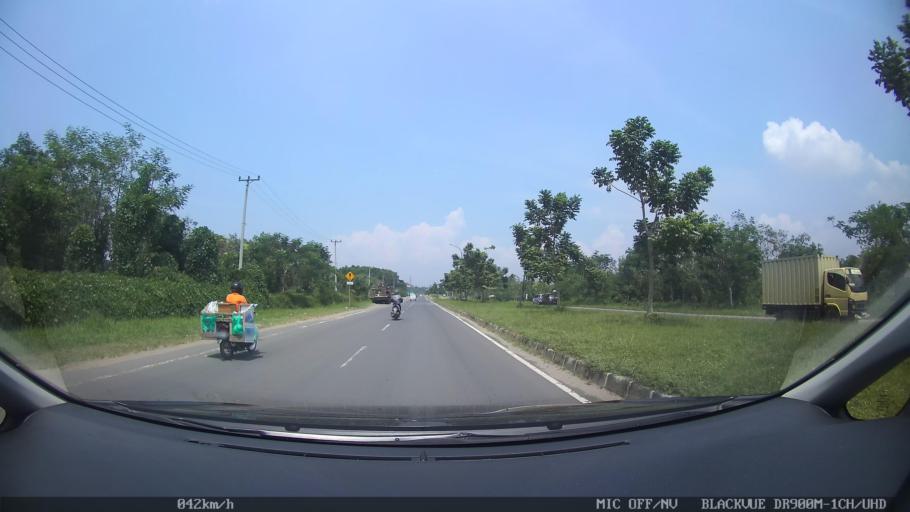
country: ID
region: Lampung
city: Kedaton
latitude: -5.3547
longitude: 105.3198
